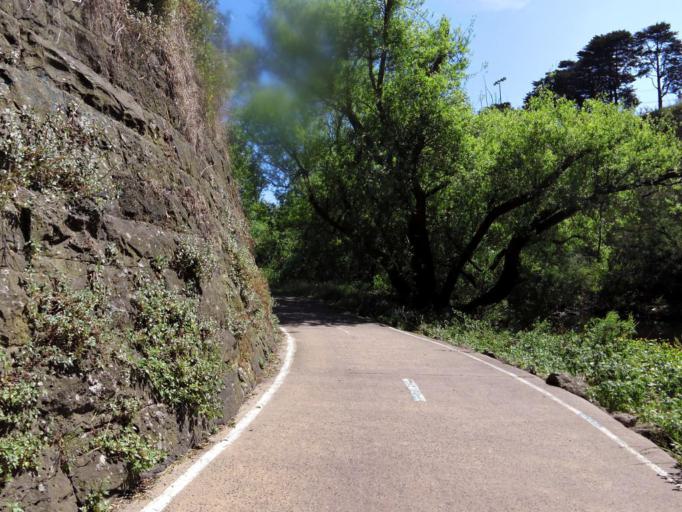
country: AU
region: Victoria
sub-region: Darebin
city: Fairfield
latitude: -37.7843
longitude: 145.0041
